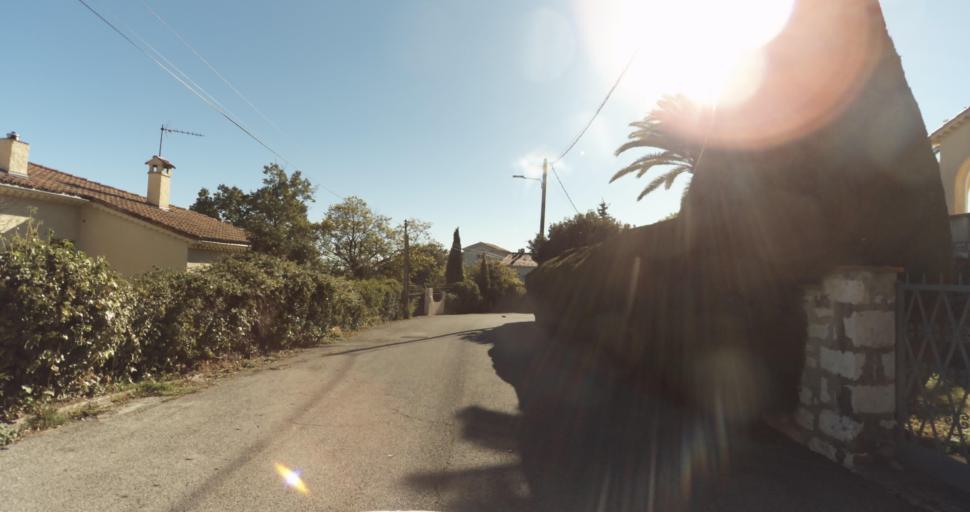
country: FR
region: Provence-Alpes-Cote d'Azur
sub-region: Departement des Alpes-Maritimes
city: Vence
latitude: 43.7183
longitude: 7.1108
